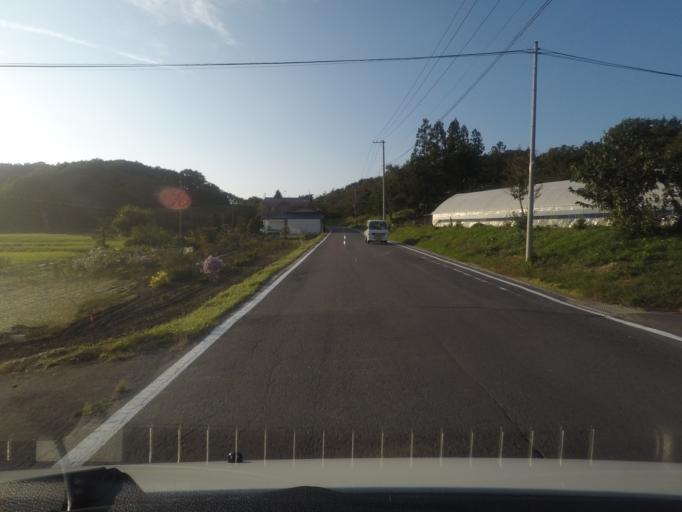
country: JP
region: Fukushima
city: Funehikimachi-funehiki
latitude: 37.6174
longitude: 140.6511
